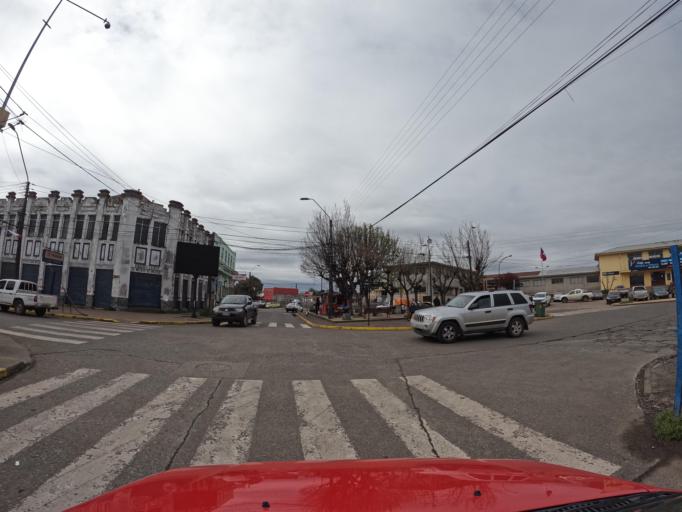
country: CL
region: Araucania
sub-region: Provincia de Malleco
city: Victoria
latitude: -38.2366
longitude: -72.3336
